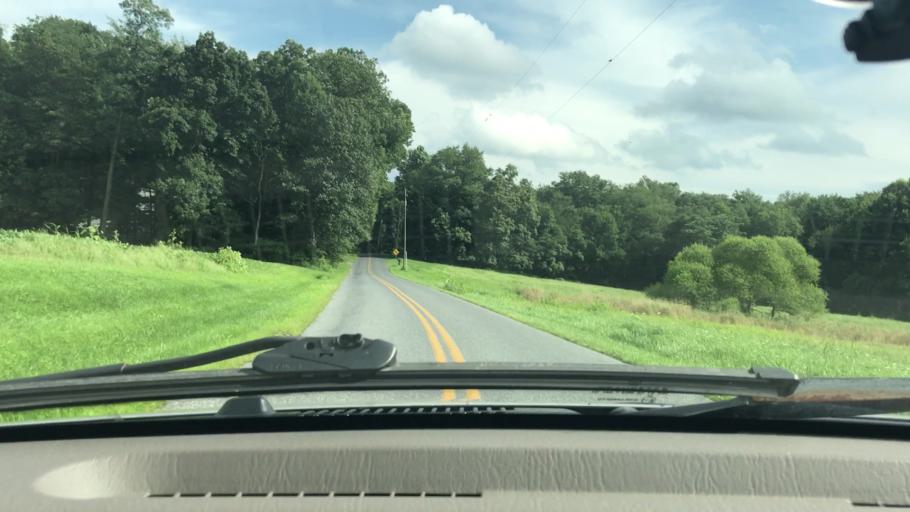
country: US
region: Pennsylvania
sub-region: Lancaster County
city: Elizabethtown
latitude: 40.1732
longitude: -76.6171
